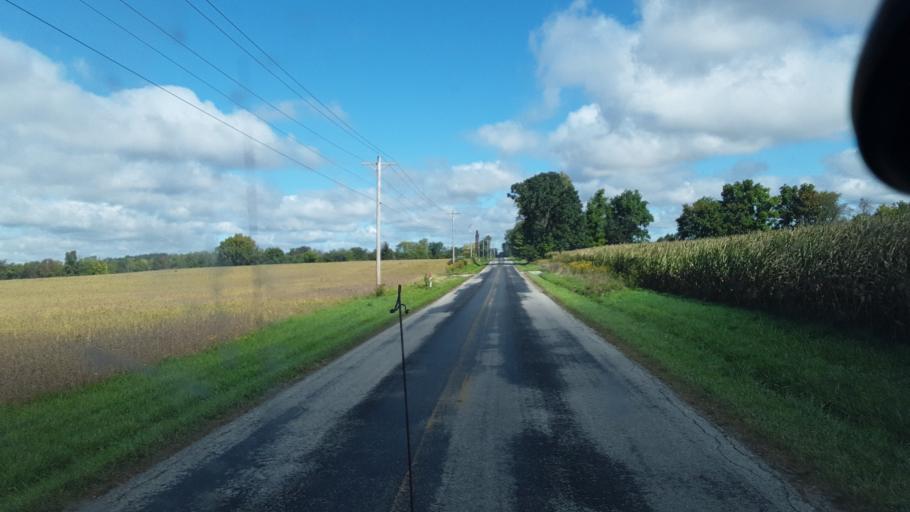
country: US
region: Ohio
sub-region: Licking County
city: Johnstown
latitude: 40.2176
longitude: -82.7552
